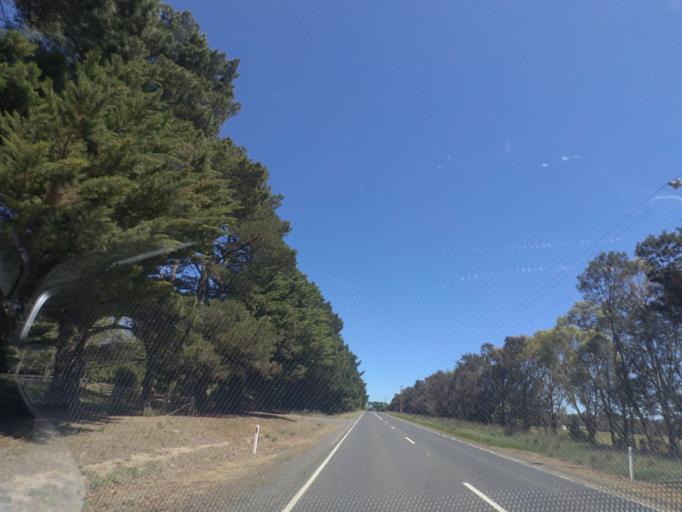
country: AU
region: Victoria
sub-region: Hume
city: Sunbury
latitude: -37.2849
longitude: 144.7642
